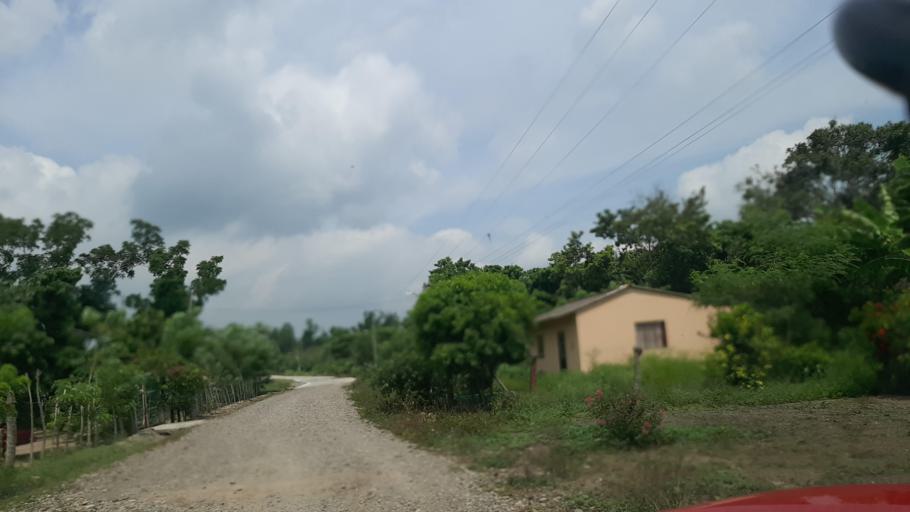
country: MX
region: Veracruz
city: Gutierrez Zamora
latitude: 20.4453
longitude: -97.1661
